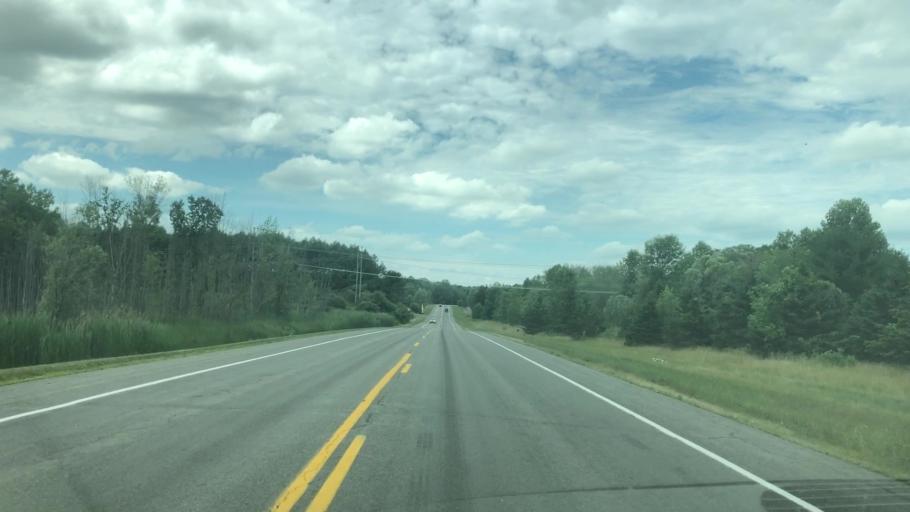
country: US
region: New York
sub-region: Wayne County
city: Macedon
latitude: 43.1237
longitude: -77.3269
